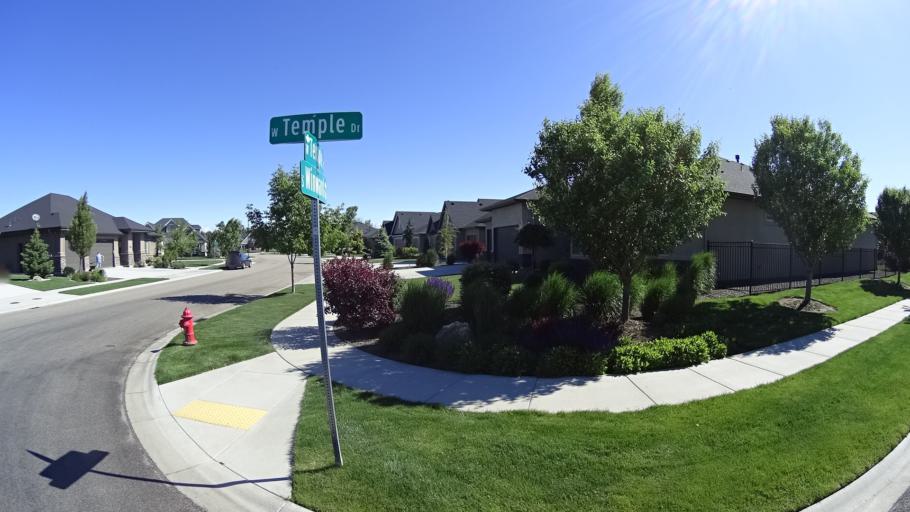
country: US
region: Idaho
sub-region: Ada County
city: Eagle
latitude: 43.6678
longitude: -116.3991
